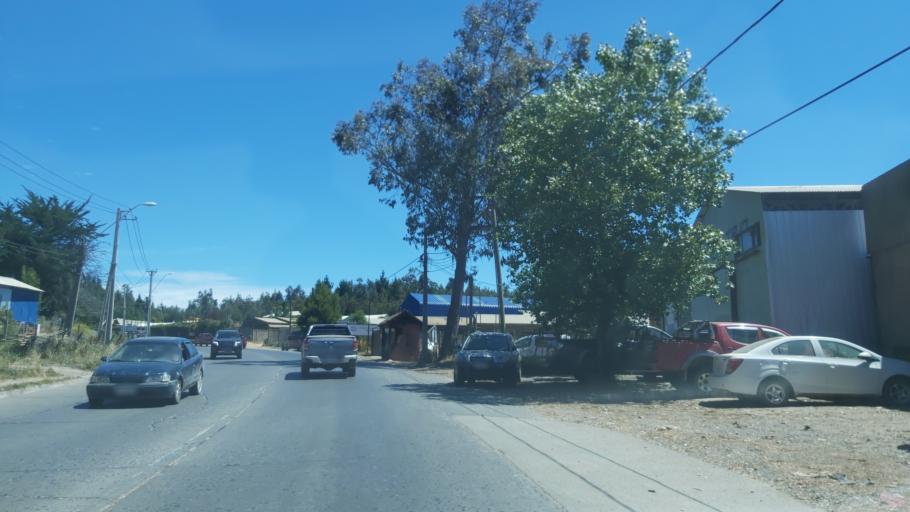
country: CL
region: Maule
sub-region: Provincia de Talca
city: Constitucion
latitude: -35.3519
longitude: -72.4096
